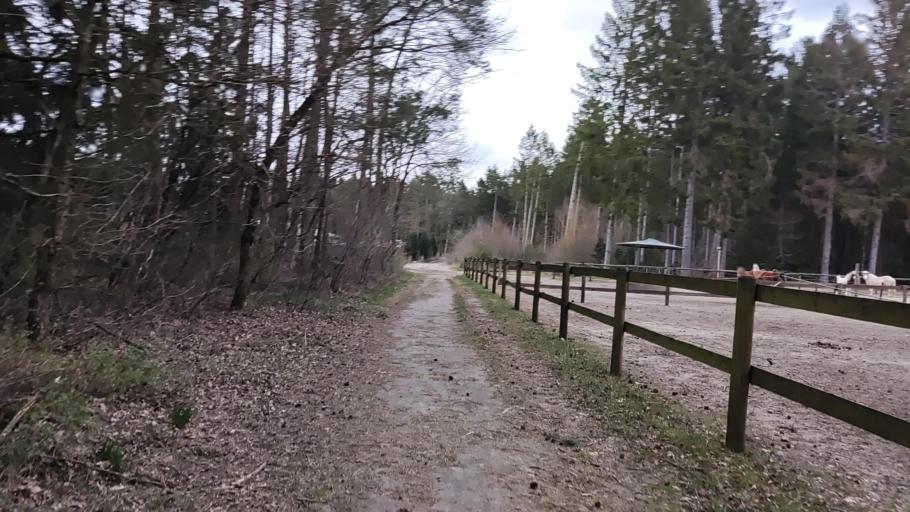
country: DE
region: Lower Saxony
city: Jesteburg
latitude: 53.2875
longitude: 9.9439
